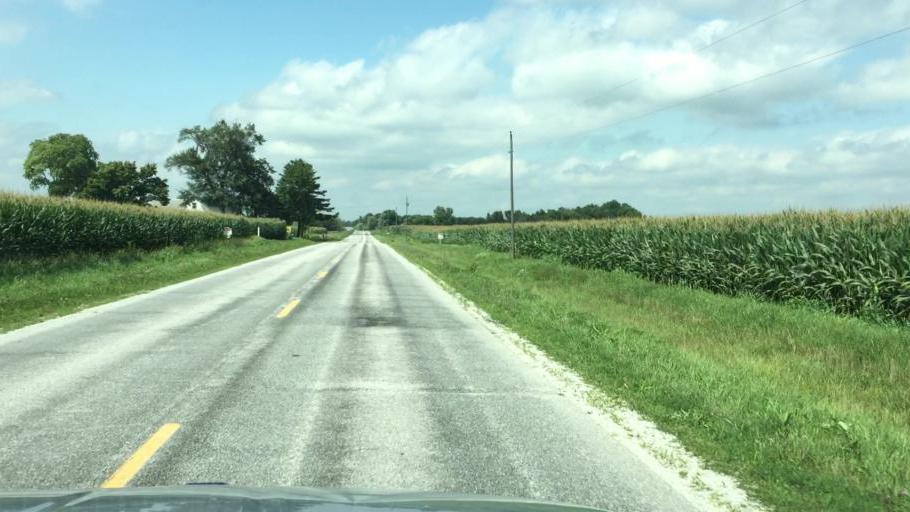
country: US
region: Illinois
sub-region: Hancock County
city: Nauvoo
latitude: 40.5163
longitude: -91.3080
